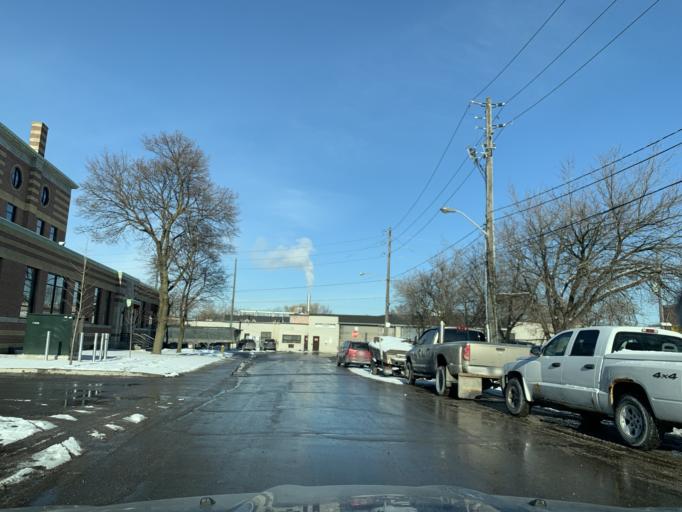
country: CA
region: Ontario
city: Toronto
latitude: 43.6731
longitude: -79.4778
